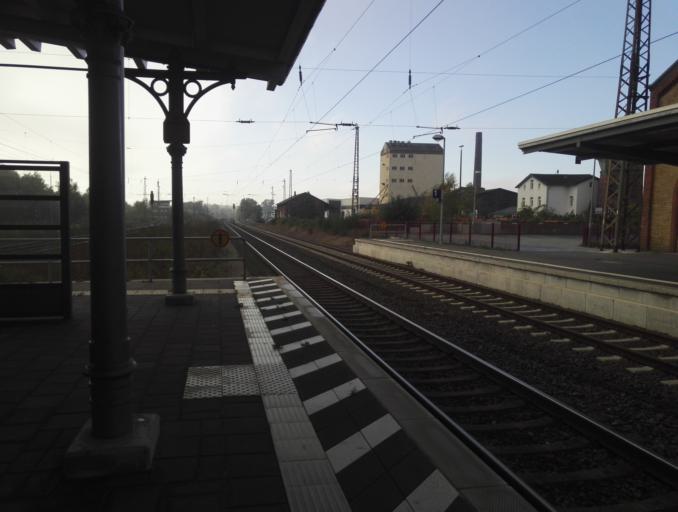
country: DE
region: Lower Saxony
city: Elze
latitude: 52.1201
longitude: 9.7467
